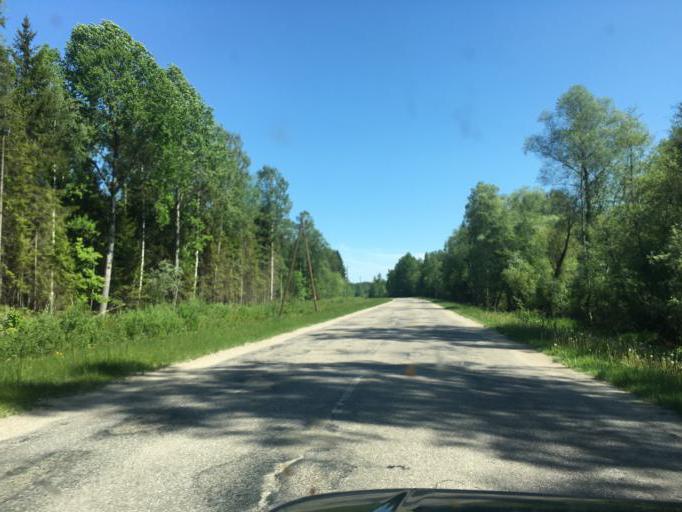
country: LV
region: Talsu Rajons
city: Valdemarpils
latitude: 57.4434
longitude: 22.6369
